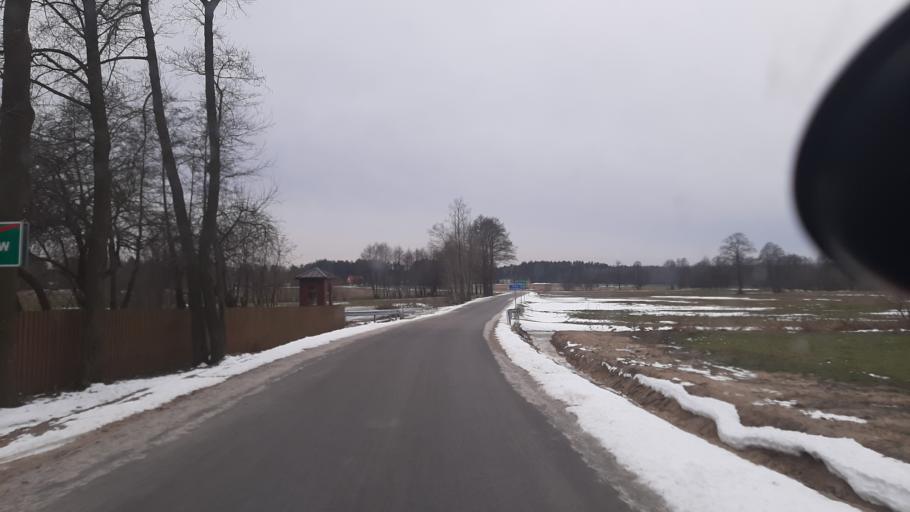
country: PL
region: Lublin Voivodeship
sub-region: Powiat lubartowski
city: Kamionka
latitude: 51.5096
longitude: 22.4583
